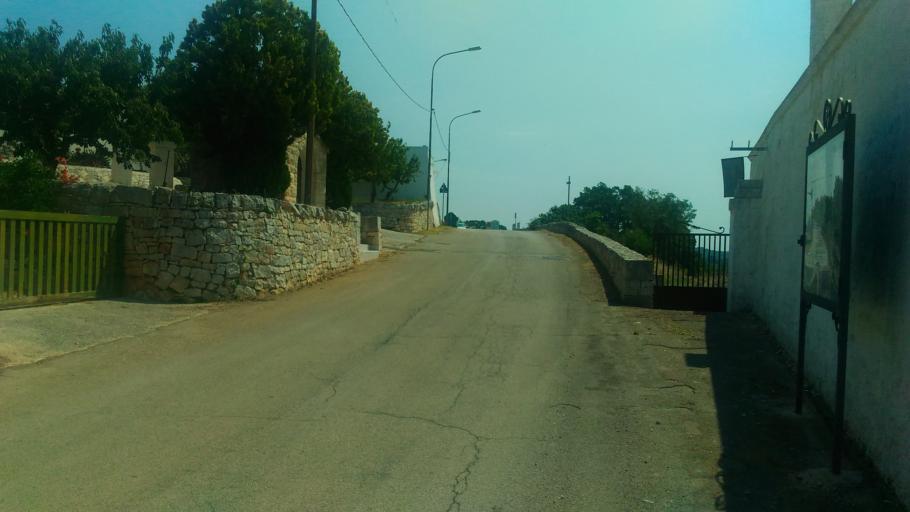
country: IT
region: Apulia
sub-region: Provincia di Brindisi
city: Cisternino
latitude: 40.7472
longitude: 17.3750
